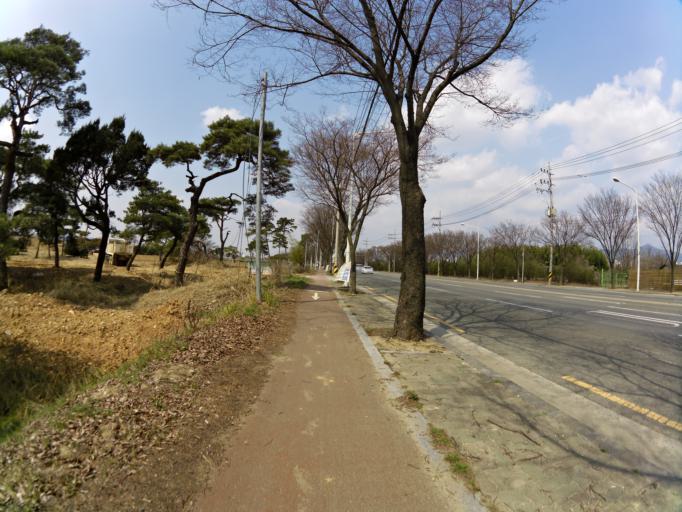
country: KR
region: Gyeongsangbuk-do
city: Gyeongsan-si
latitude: 35.8569
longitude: 128.7207
